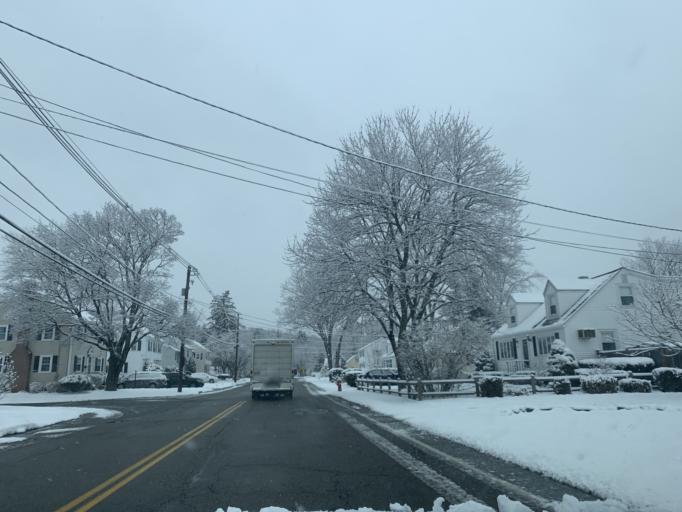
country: US
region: Massachusetts
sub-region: Norfolk County
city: Norwood
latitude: 42.2052
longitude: -71.1927
